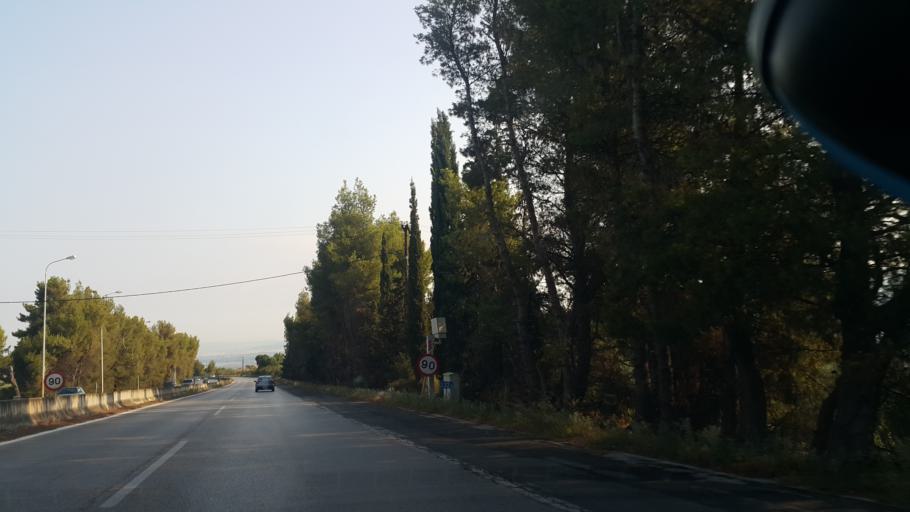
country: GR
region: Central Macedonia
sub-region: Nomos Thessalonikis
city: Kardia
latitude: 40.4632
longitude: 22.9981
